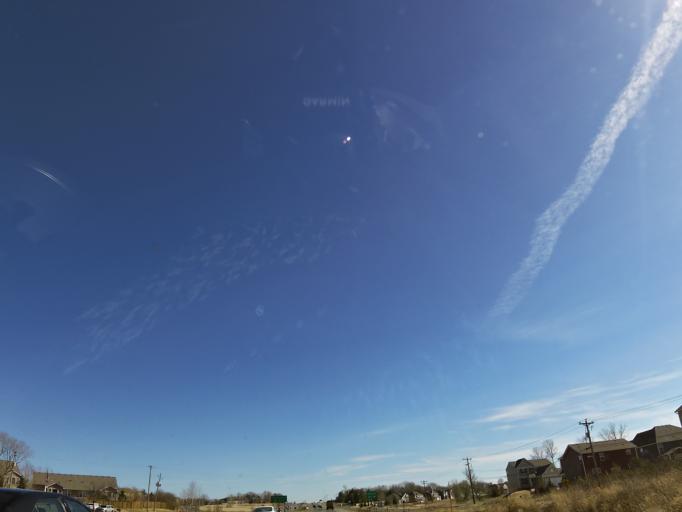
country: US
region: Minnesota
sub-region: Hennepin County
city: Corcoran
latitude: 45.0401
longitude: -93.5193
